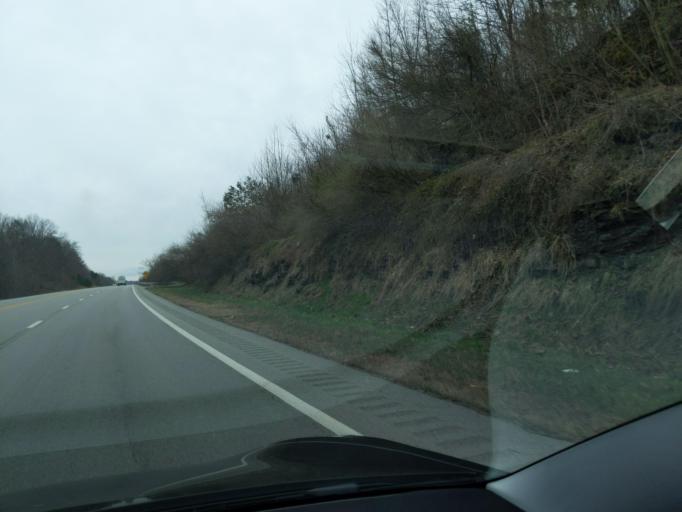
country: US
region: Kentucky
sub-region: Whitley County
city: Corbin
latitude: 36.9158
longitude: -84.0796
